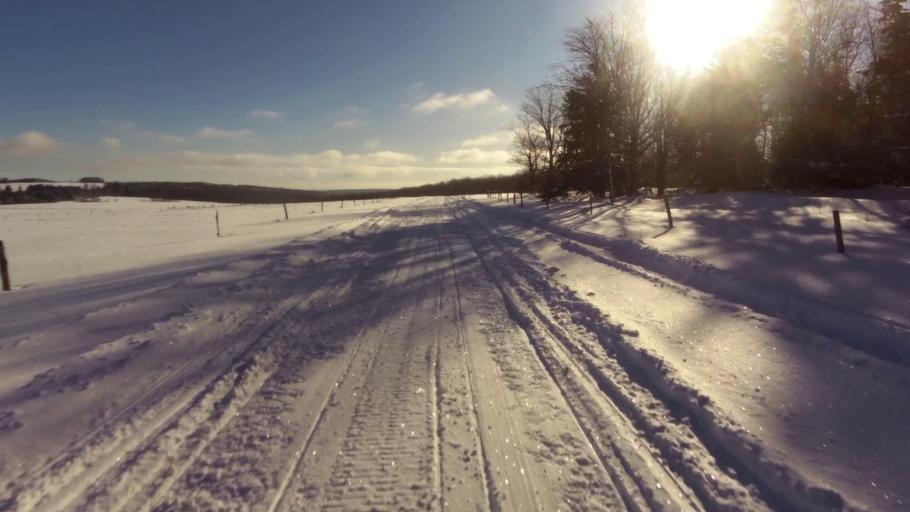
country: US
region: New York
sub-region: Chautauqua County
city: Falconer
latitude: 42.2554
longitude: -79.2080
